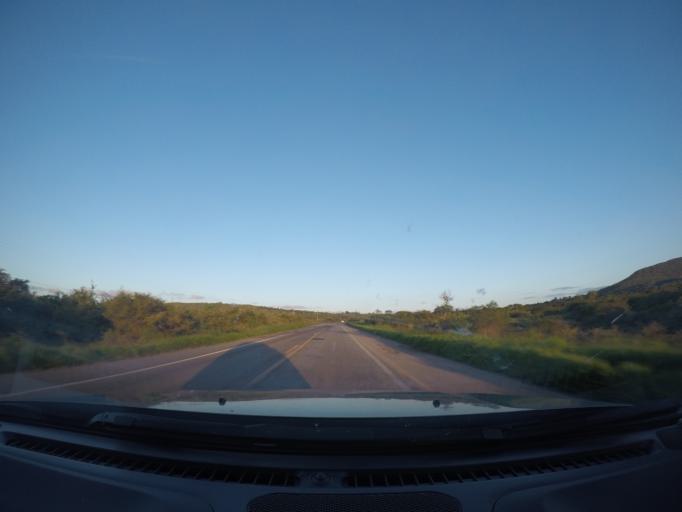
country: BR
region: Bahia
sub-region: Seabra
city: Seabra
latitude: -12.3891
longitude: -41.8925
